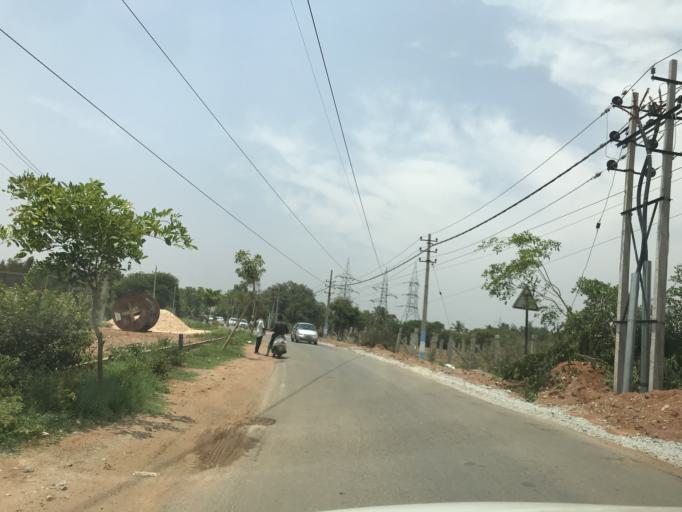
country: IN
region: Karnataka
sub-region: Bangalore Rural
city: Devanhalli
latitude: 13.1811
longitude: 77.6680
